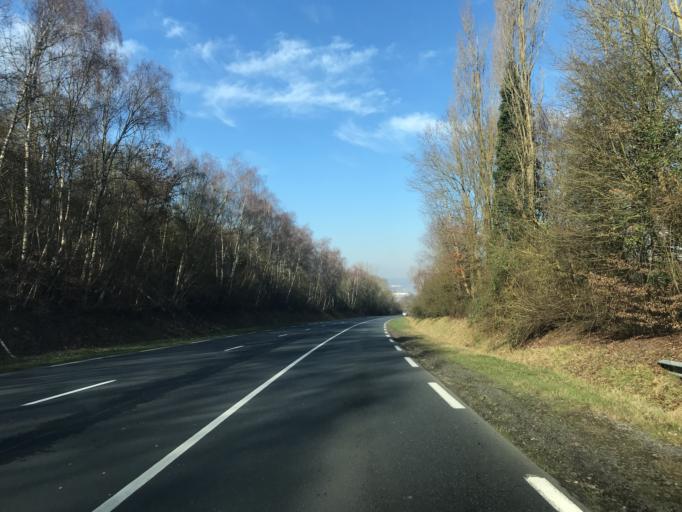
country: FR
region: Haute-Normandie
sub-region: Departement de l'Eure
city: Saint-Pierre-du-Vauvray
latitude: 49.2317
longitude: 1.2074
